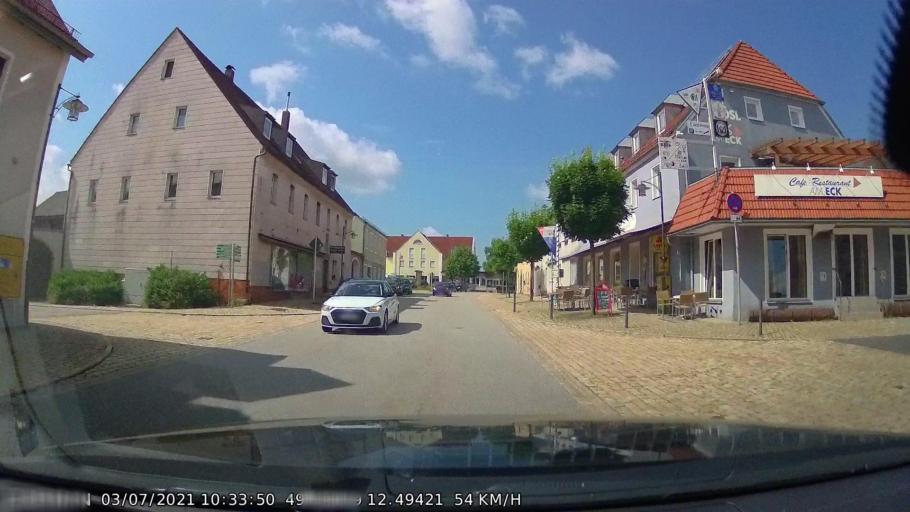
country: DE
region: Bavaria
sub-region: Upper Palatinate
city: Waidhaus
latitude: 49.6413
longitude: 12.4940
